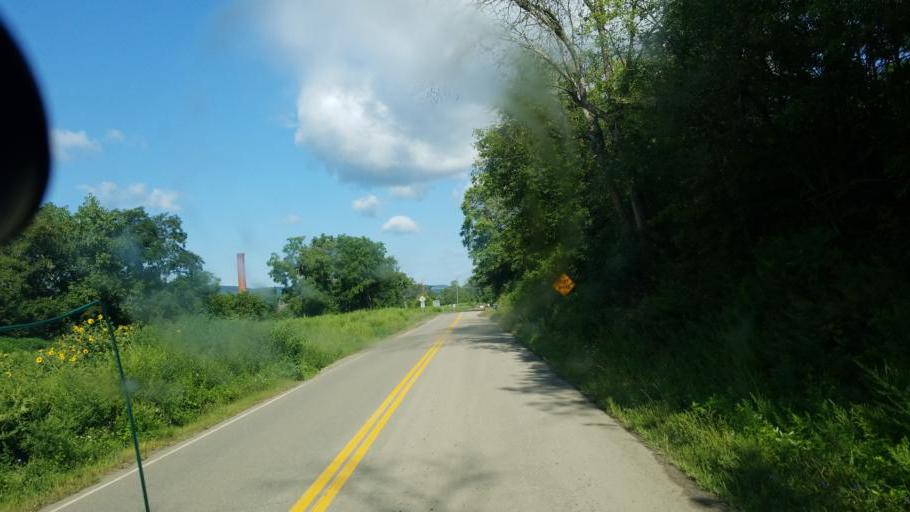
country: US
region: New York
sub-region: Steuben County
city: Canisteo
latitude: 42.2761
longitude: -77.5984
